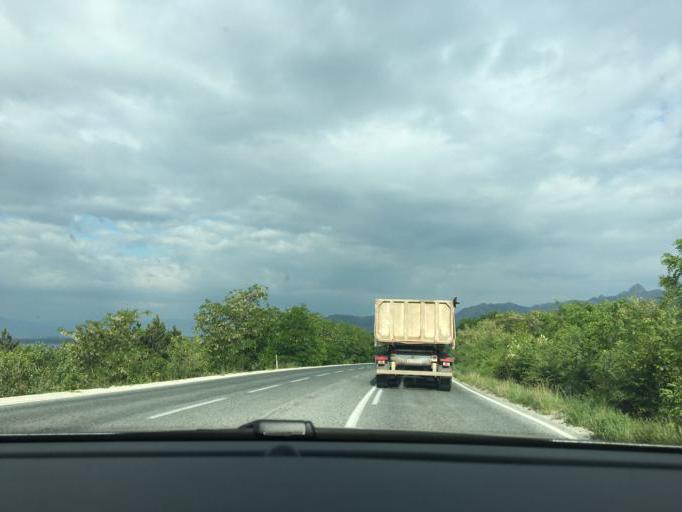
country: MK
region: Prilep
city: Prilep
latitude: 41.3691
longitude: 21.6299
